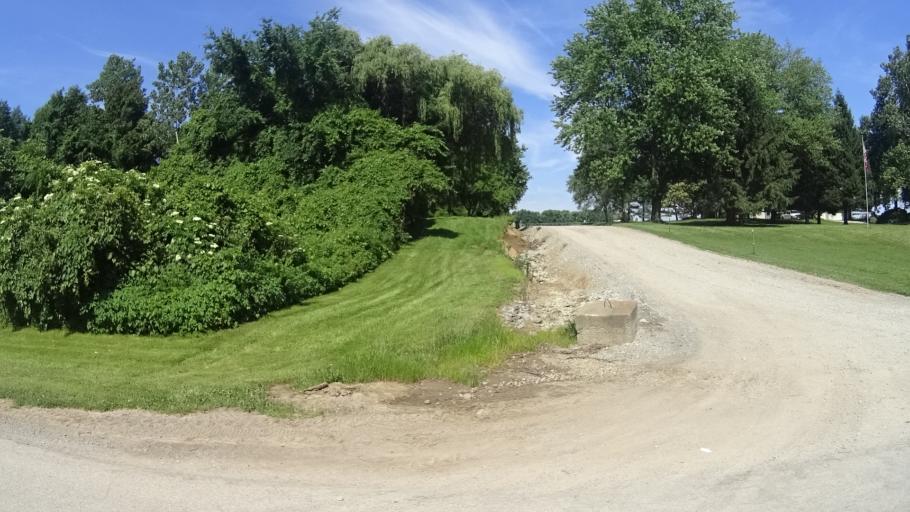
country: US
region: Ohio
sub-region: Erie County
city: Huron
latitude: 41.3704
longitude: -82.4719
